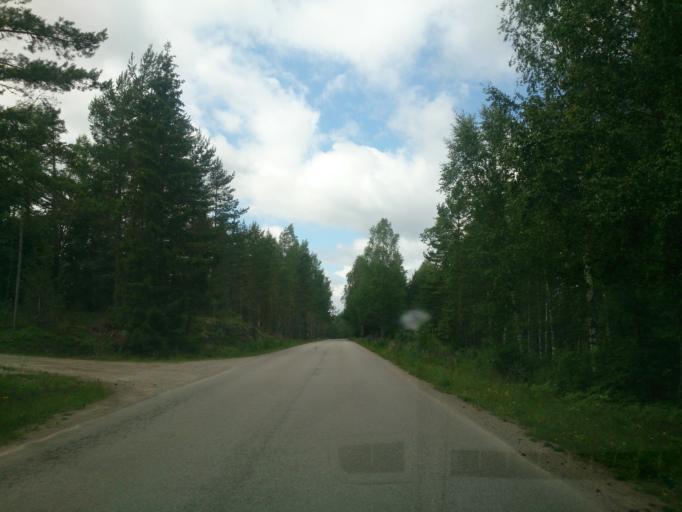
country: SE
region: OEstergoetland
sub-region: Norrkopings Kommun
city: Jursla
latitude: 58.7265
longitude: 16.1174
